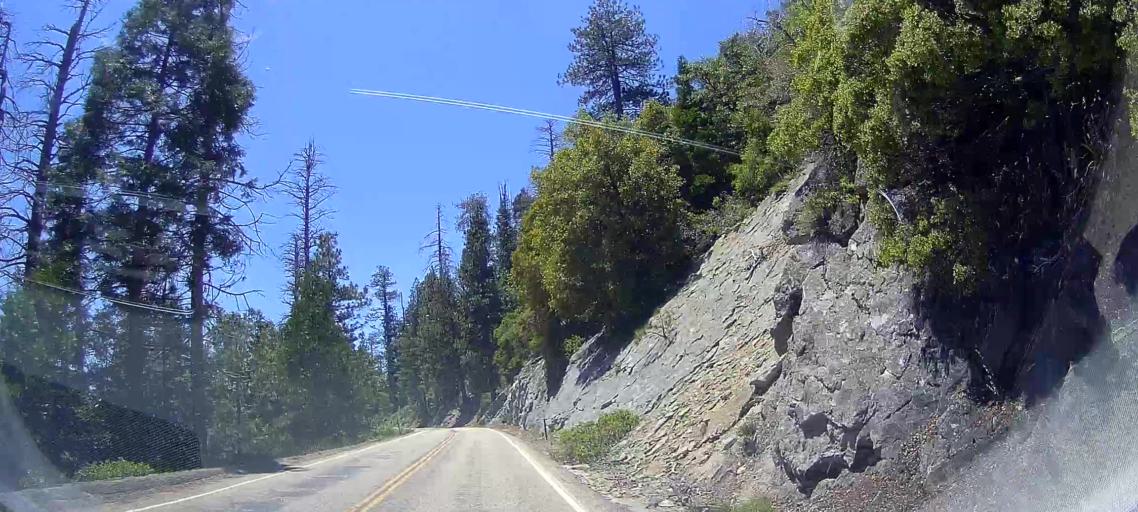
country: US
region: California
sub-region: Tulare County
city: Three Rivers
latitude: 36.7169
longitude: -118.9376
